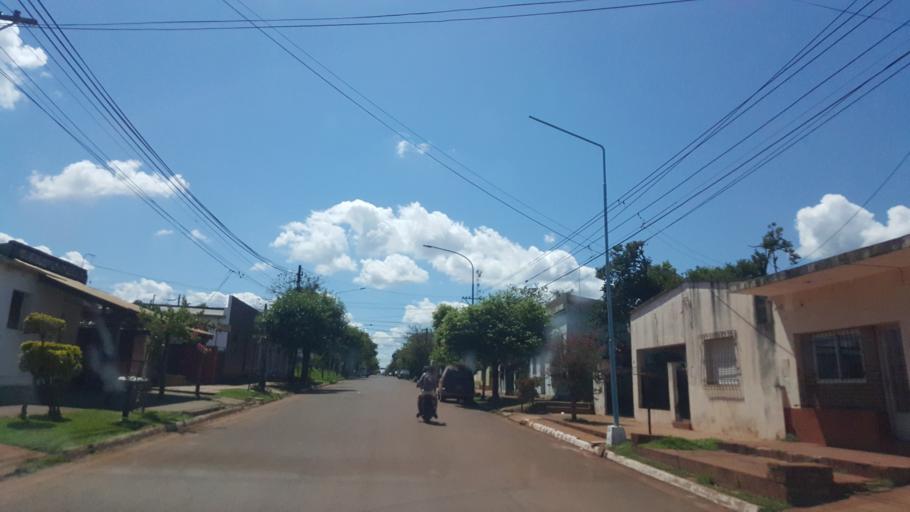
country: AR
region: Corrientes
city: Santo Tome
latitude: -28.5461
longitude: -56.0465
